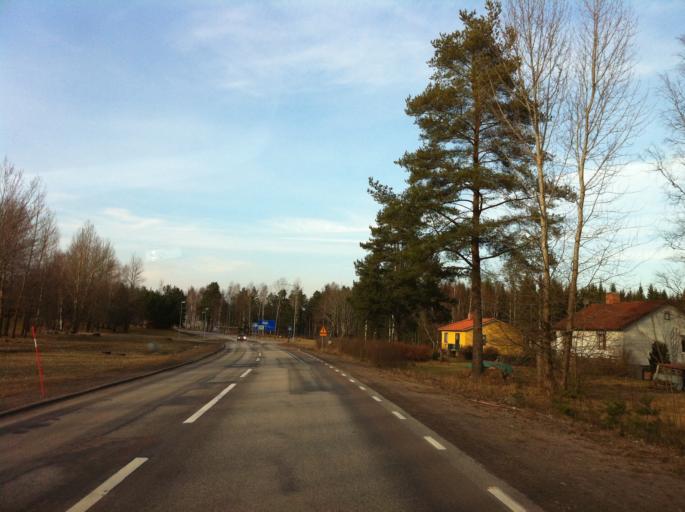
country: SE
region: Vaermland
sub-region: Storfors Kommun
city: Storfors
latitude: 59.5320
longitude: 14.2837
